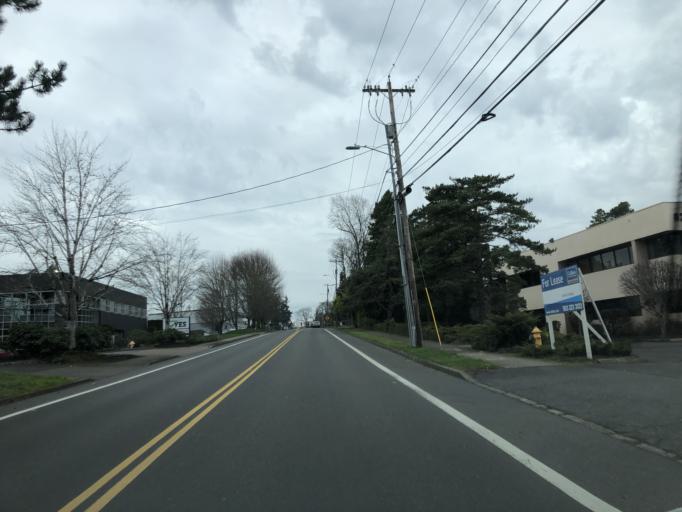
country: US
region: Oregon
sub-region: Washington County
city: Tigard
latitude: 45.4290
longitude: -122.7616
